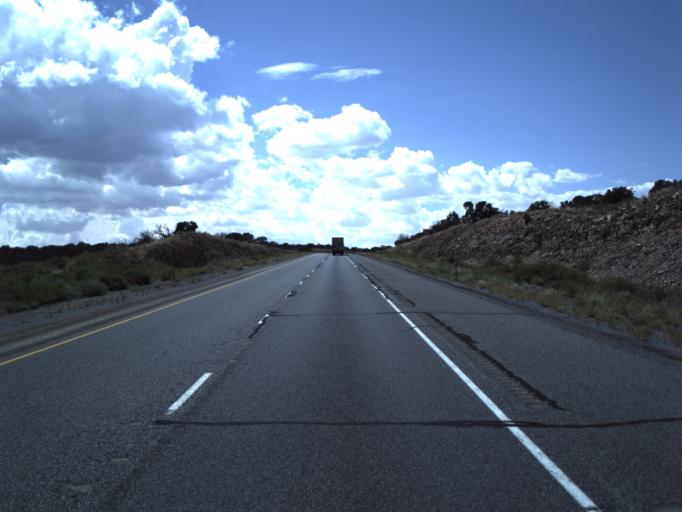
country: US
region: Utah
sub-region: Emery County
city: Castle Dale
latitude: 38.9001
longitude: -110.5718
